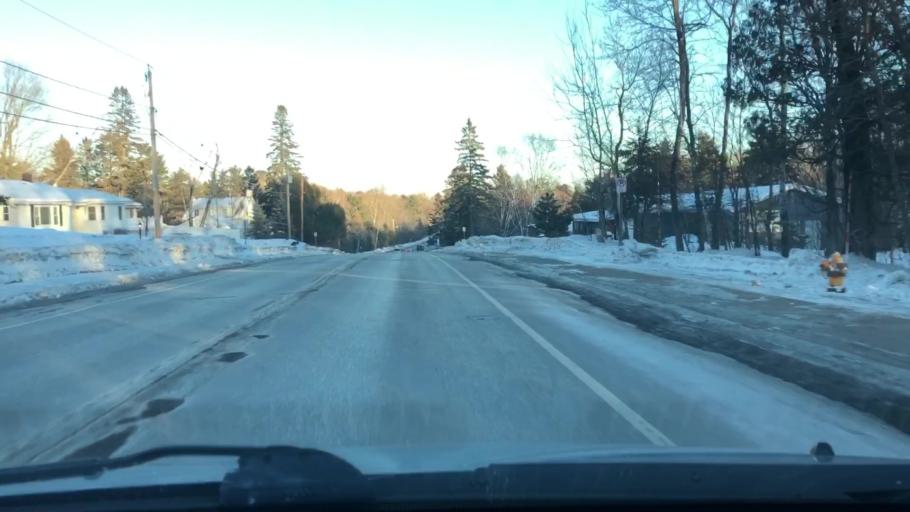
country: US
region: Minnesota
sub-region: Saint Louis County
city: Duluth
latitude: 46.8255
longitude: -92.0883
